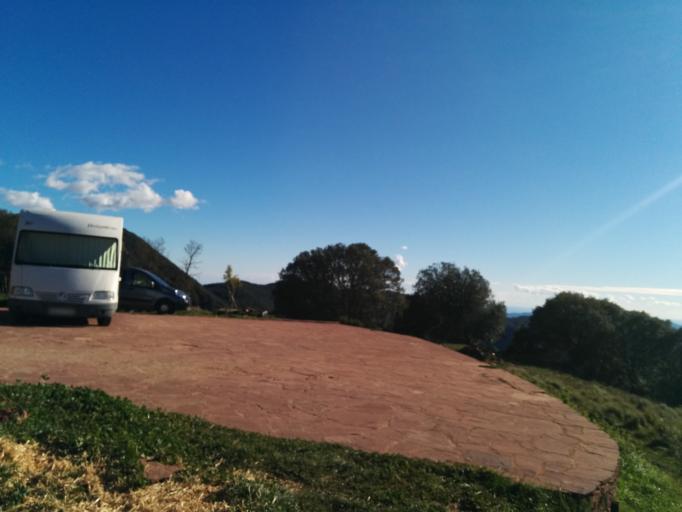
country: ES
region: Catalonia
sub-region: Provincia de Barcelona
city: Tagamanent
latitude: 41.7470
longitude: 2.3030
